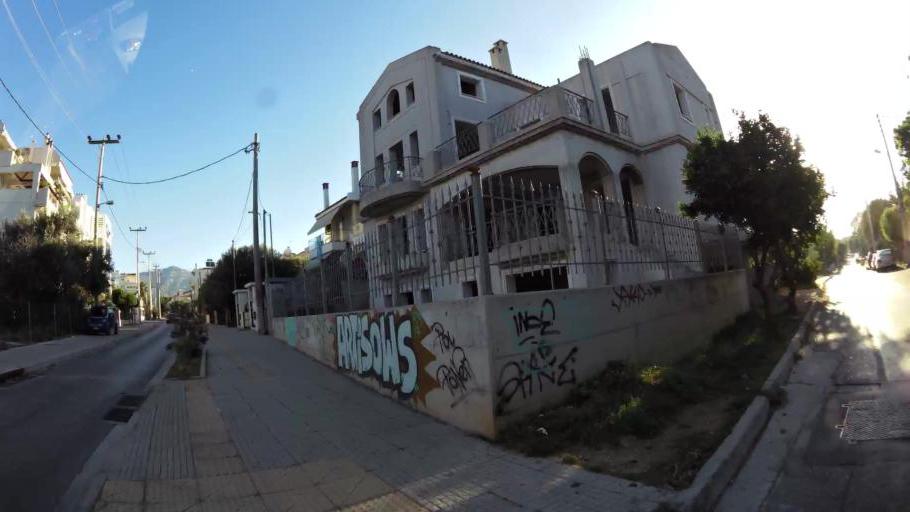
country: GR
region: Attica
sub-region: Nomarchia Athinas
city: Vrilissia
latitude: 38.0270
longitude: 23.8353
